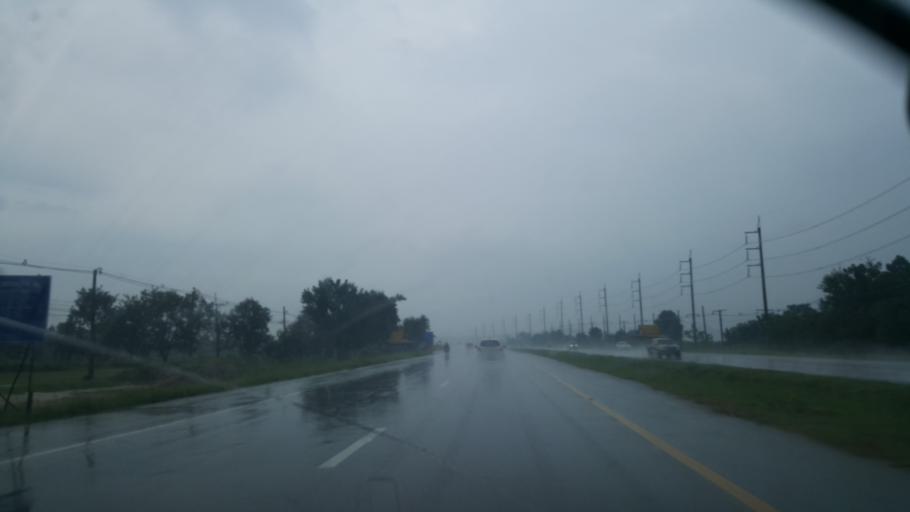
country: TH
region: Chon Buri
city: Phatthaya
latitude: 12.9223
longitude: 101.0325
